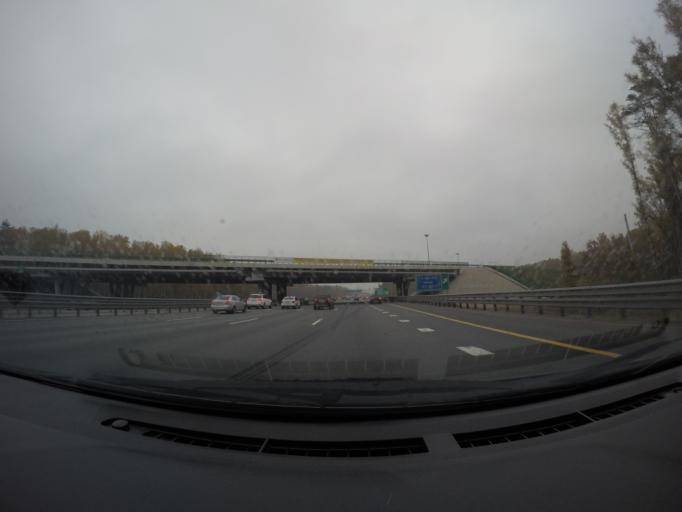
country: RU
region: Moskovskaya
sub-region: Podol'skiy Rayon
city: Podol'sk
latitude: 55.4041
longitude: 37.6058
